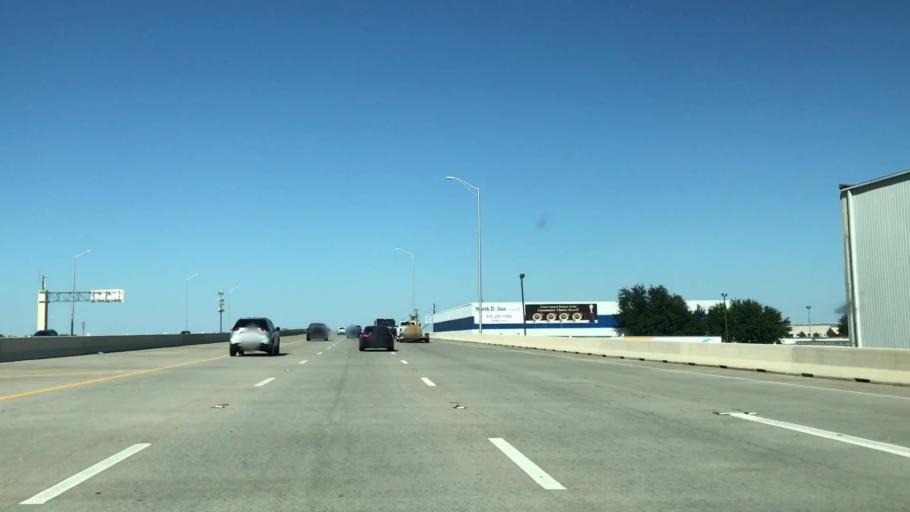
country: US
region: Texas
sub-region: Dallas County
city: Farmers Branch
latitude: 32.9218
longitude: -96.9323
